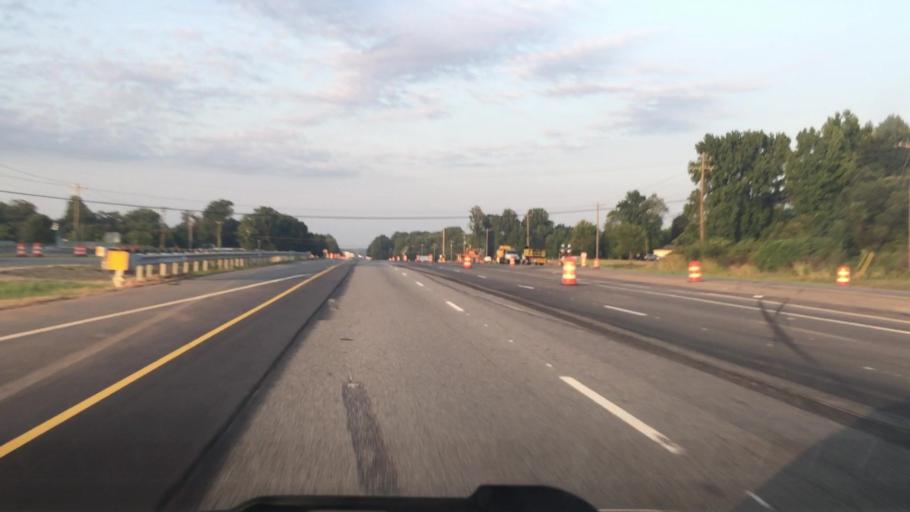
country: US
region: North Carolina
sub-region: Guilford County
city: McLeansville
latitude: 36.1400
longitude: -79.7382
